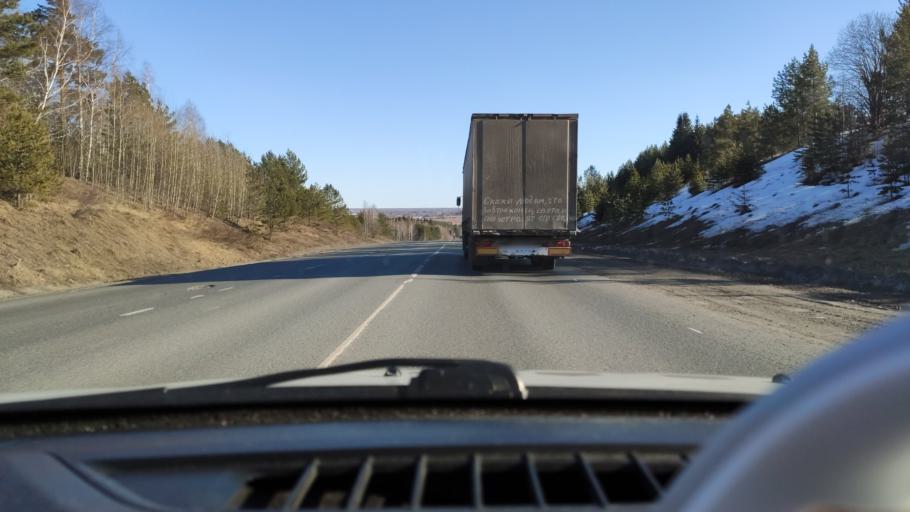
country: RU
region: Perm
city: Kungur
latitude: 57.3174
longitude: 56.9685
